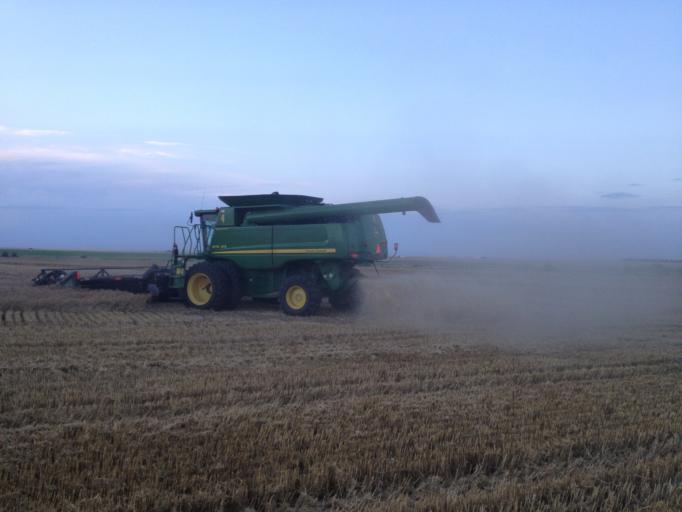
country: US
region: Oklahoma
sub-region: Alfalfa County
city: Helena
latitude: 36.6517
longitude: -98.0427
